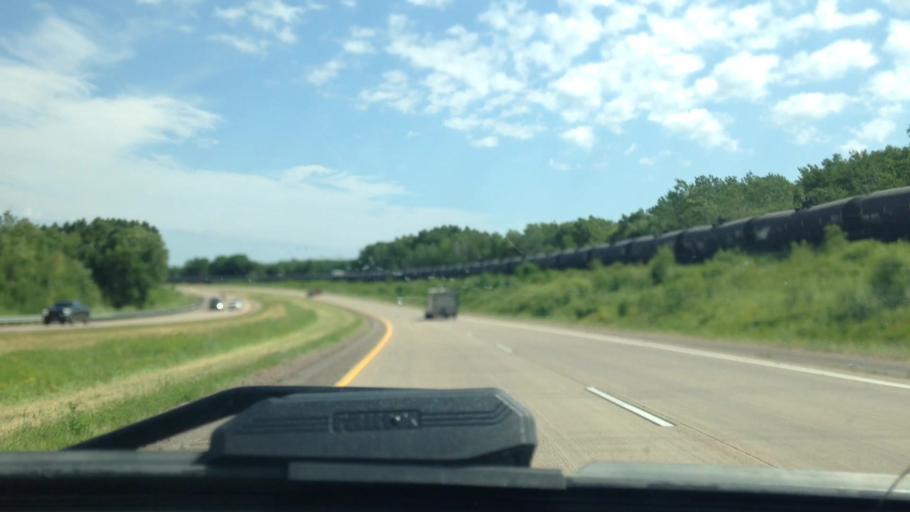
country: US
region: Wisconsin
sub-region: Washburn County
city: Spooner
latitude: 45.8648
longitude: -91.8344
